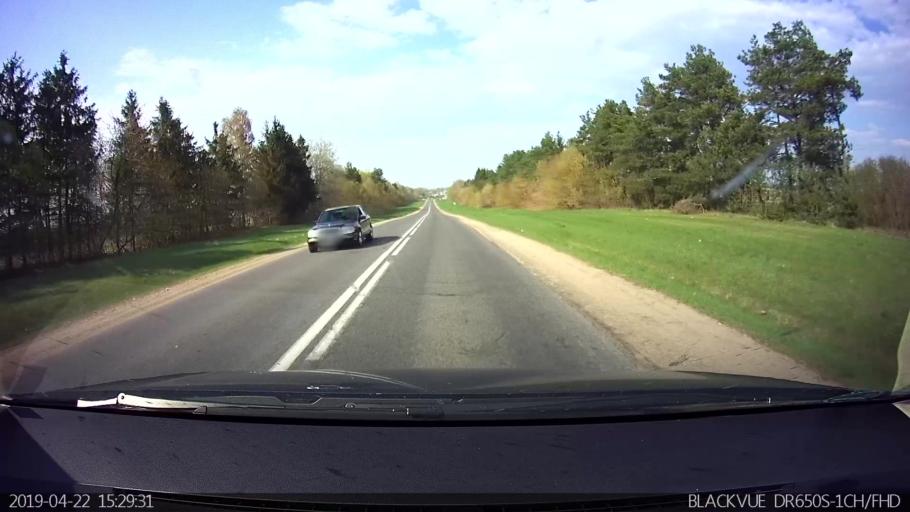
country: BY
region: Brest
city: Vysokaye
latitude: 52.3875
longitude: 23.3742
